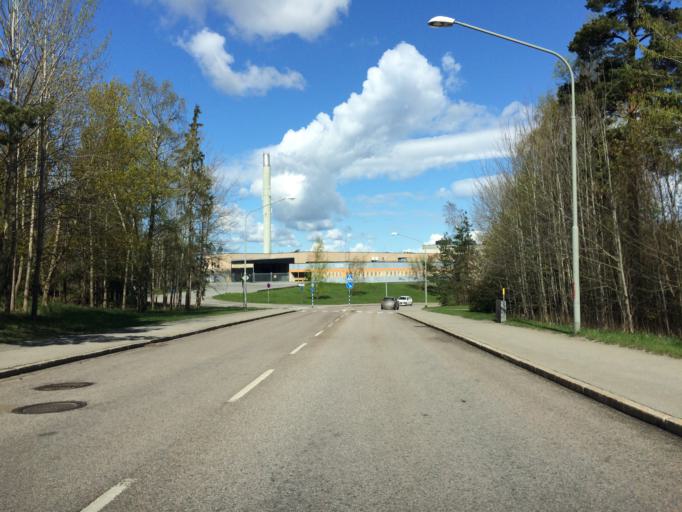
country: SE
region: Stockholm
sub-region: Huddinge Kommun
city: Segeltorp
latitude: 59.2946
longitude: 17.9447
